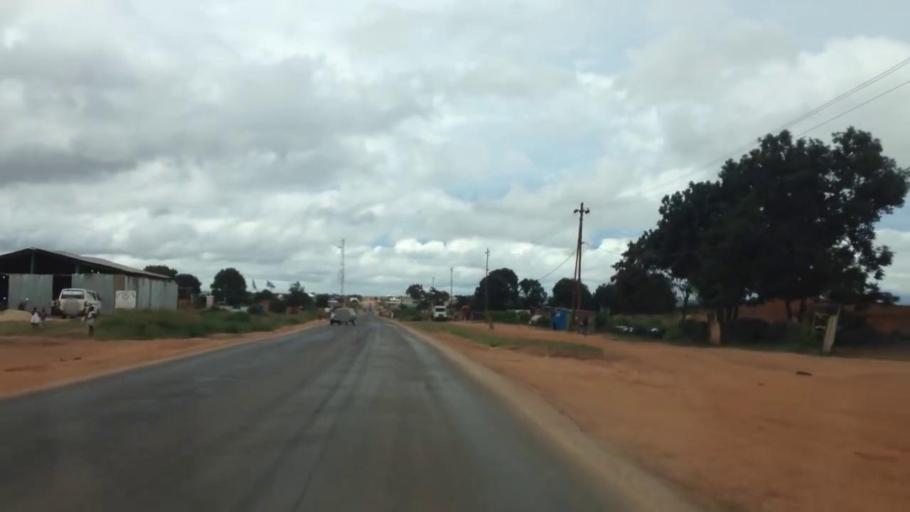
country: CD
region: Katanga
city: Kolwezi
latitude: -10.7294
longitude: 25.5094
